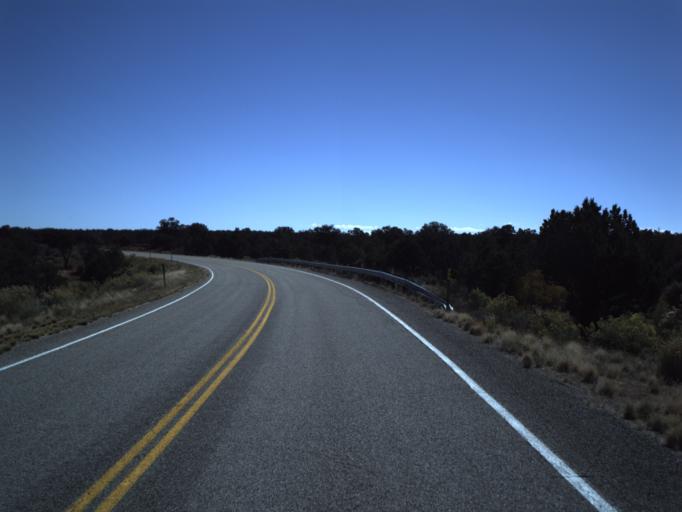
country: US
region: Utah
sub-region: San Juan County
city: Blanding
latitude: 37.5633
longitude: -110.0263
